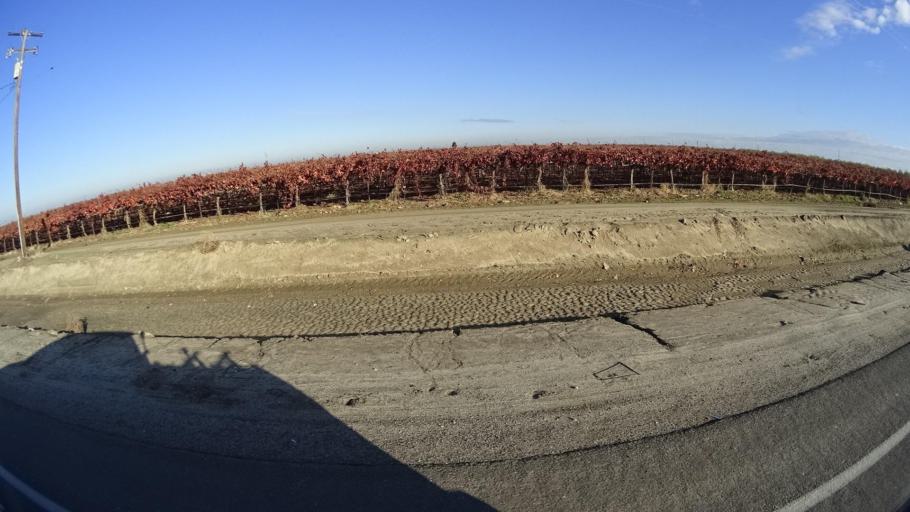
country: US
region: California
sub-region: Kern County
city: Delano
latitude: 35.7759
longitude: -119.2833
